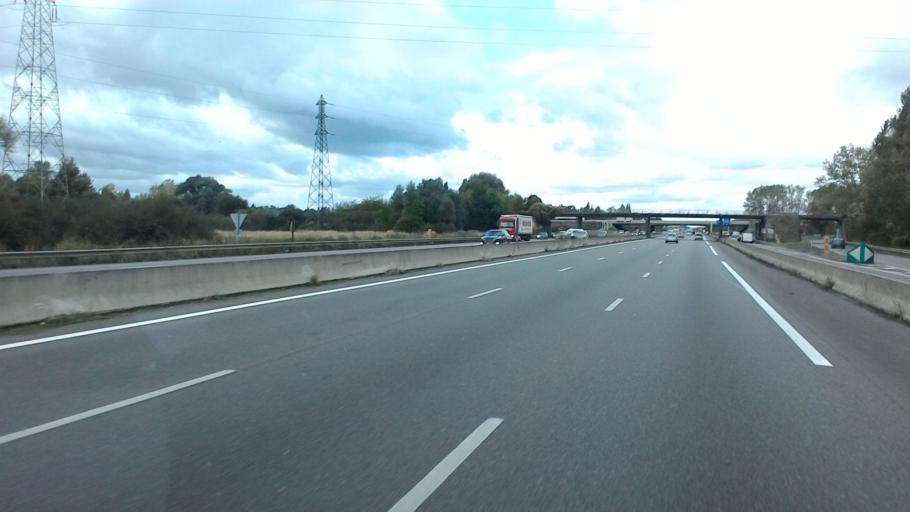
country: FR
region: Lorraine
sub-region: Departement de la Moselle
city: Maizieres-les-Metz
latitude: 49.1969
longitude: 6.1756
